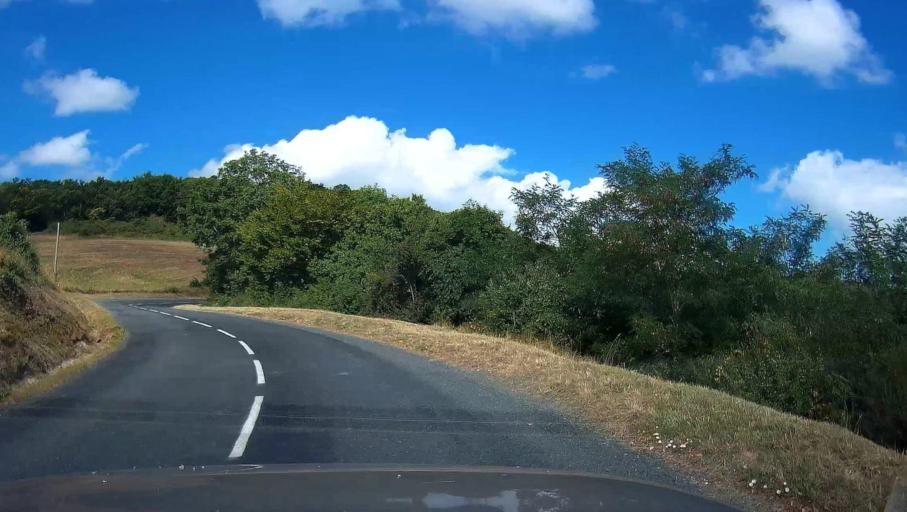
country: FR
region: Rhone-Alpes
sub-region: Departement du Rhone
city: Cogny
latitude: 45.9843
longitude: 4.5802
